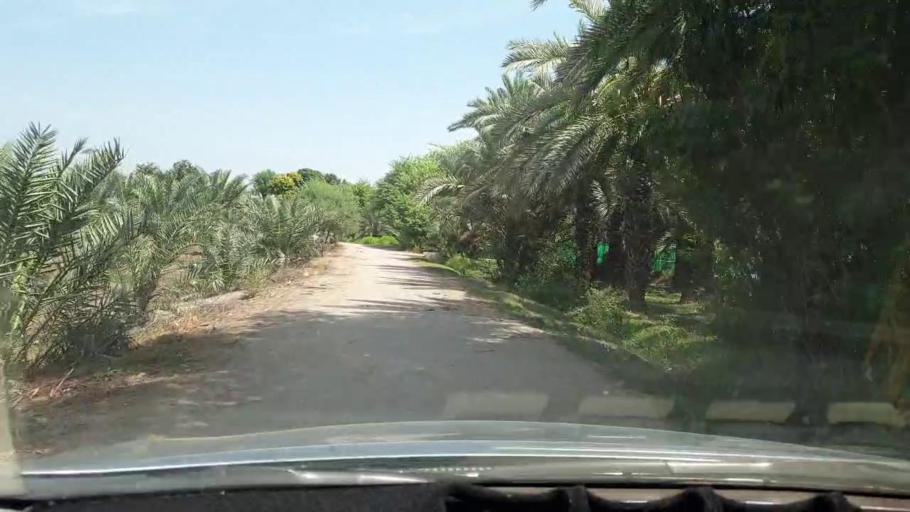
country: PK
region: Sindh
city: Khairpur
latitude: 27.4986
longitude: 68.7502
